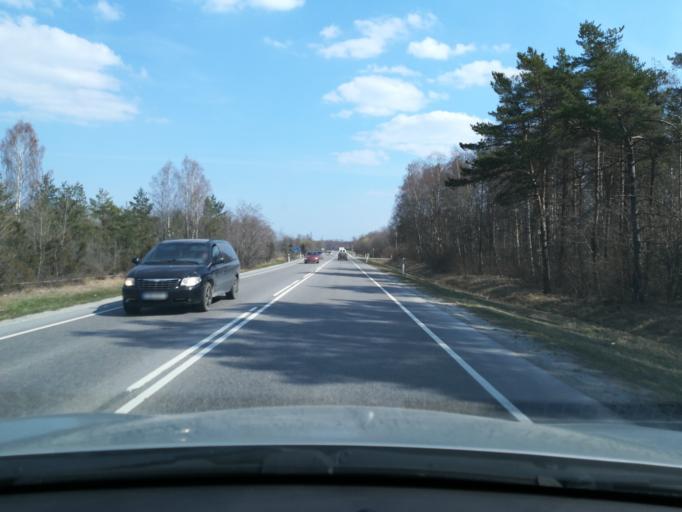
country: EE
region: Harju
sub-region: Saue linn
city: Saue
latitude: 59.3648
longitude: 24.5099
